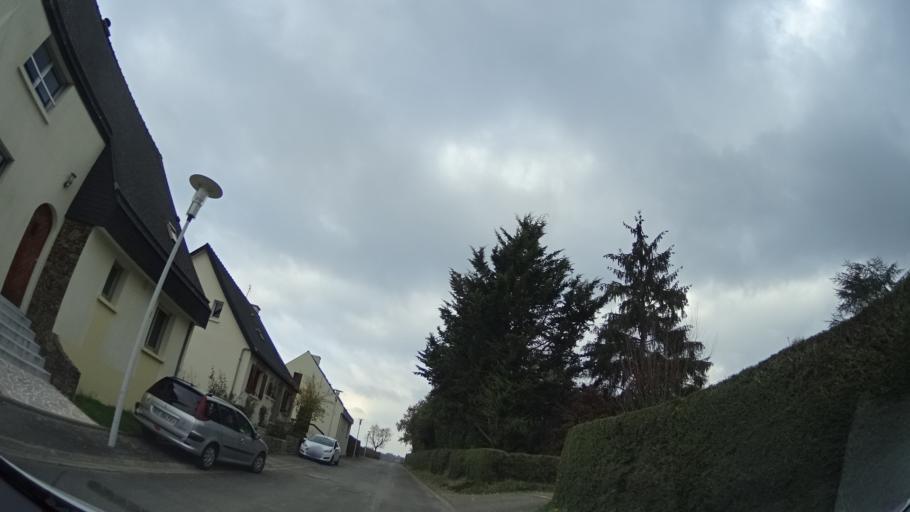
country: FR
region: Brittany
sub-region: Departement d'Ille-et-Vilaine
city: Montgermont
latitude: 48.1603
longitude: -1.7141
